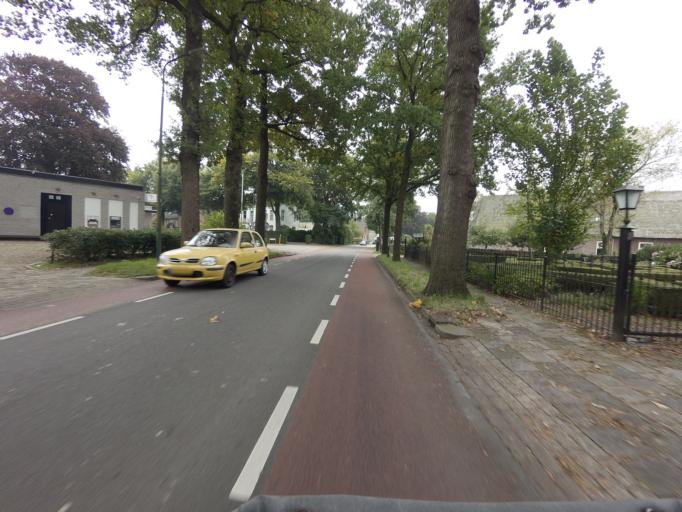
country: NL
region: North Holland
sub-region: Gemeente Wijdemeren
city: Nieuw-Loosdrecht
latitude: 52.2003
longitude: 5.1338
